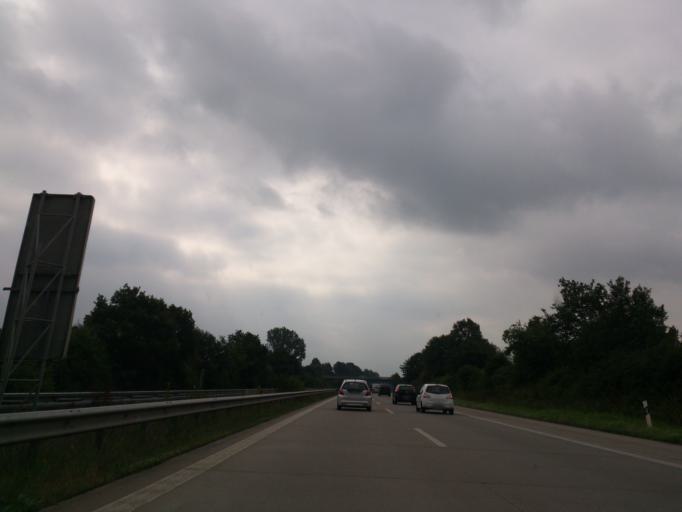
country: DE
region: Schleswig-Holstein
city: Klein Offenseth-Sparrieshoop
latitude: 53.7982
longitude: 9.6898
